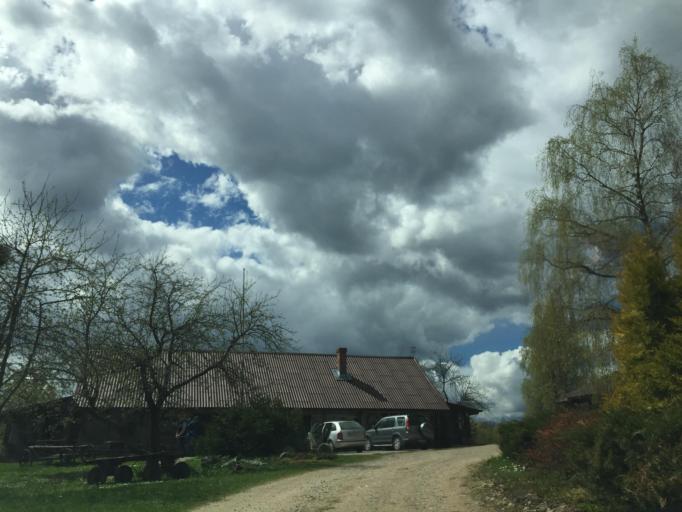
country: LV
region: Madonas Rajons
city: Madona
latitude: 56.9244
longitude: 26.0164
